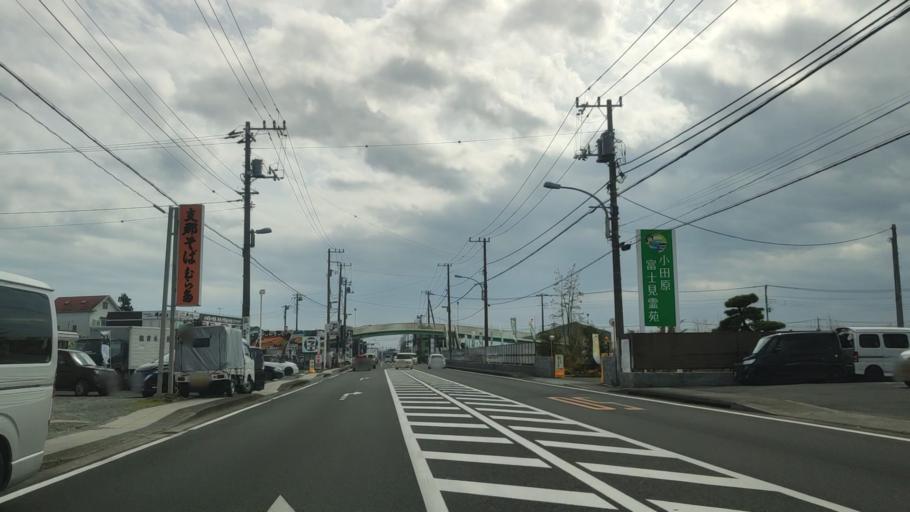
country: JP
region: Kanagawa
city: Odawara
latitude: 35.3106
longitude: 139.1634
